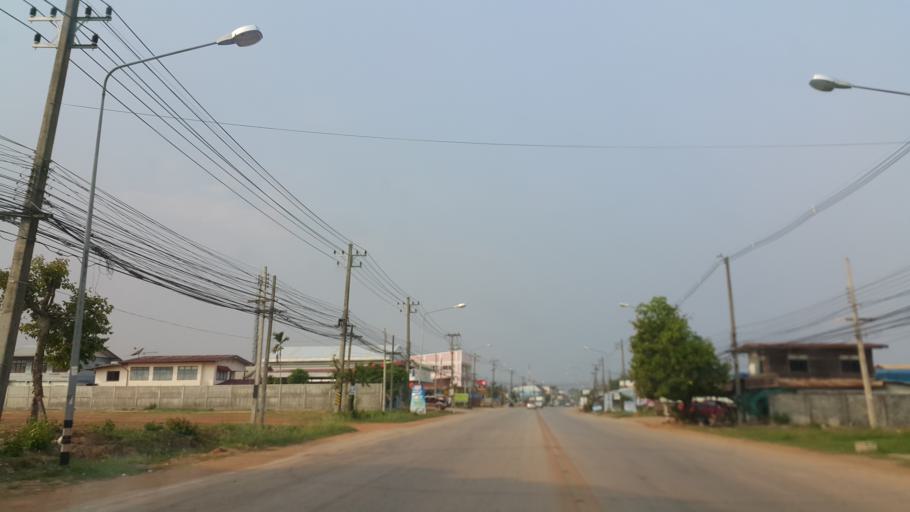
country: TH
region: Nakhon Phanom
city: That Phanom
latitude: 16.9428
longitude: 104.7209
